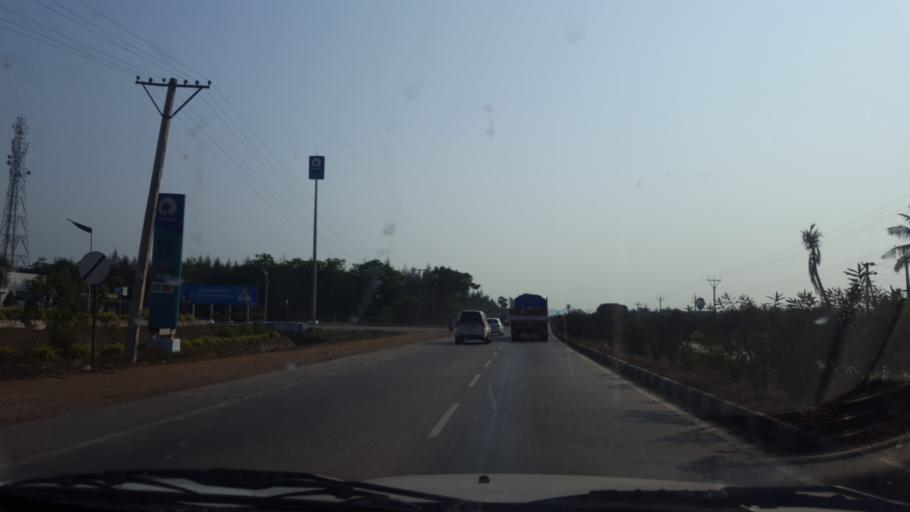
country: IN
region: Andhra Pradesh
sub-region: Vishakhapatnam
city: Elamanchili
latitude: 17.5947
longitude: 82.8720
